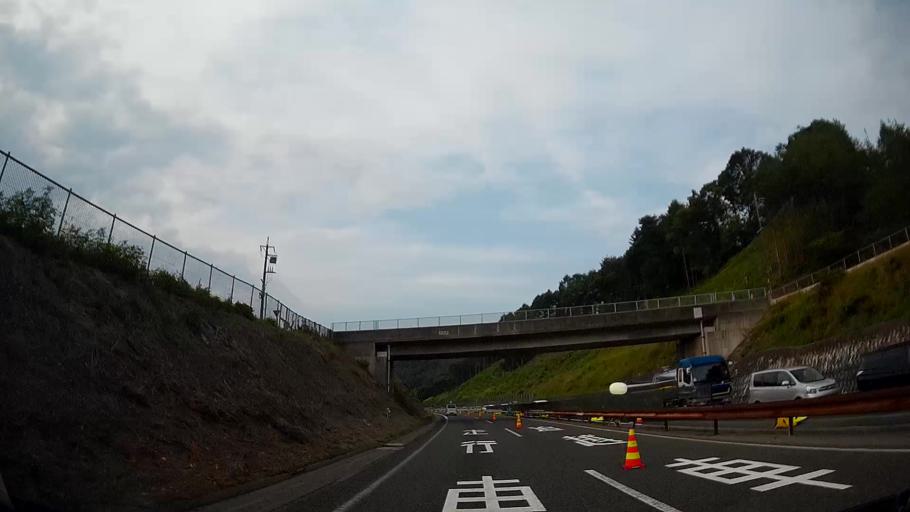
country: JP
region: Nagano
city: Tatsuno
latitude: 35.9791
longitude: 138.0062
